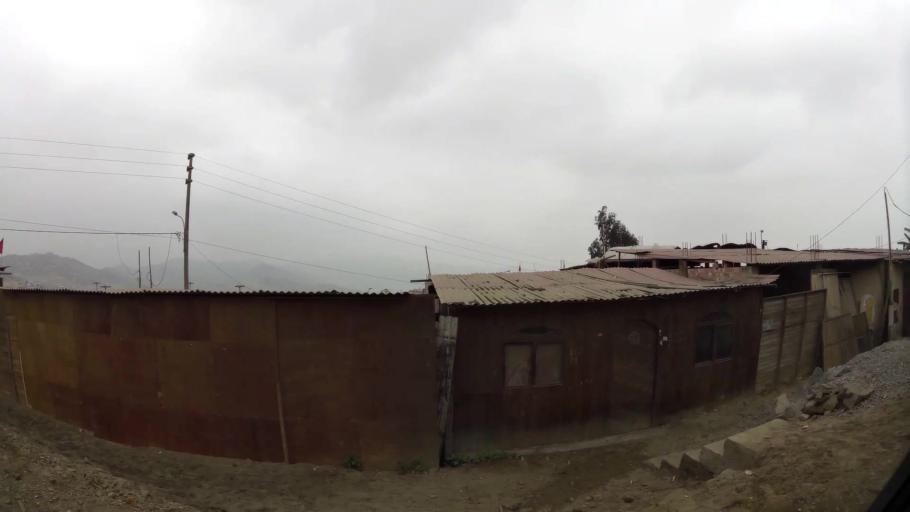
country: PE
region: Lima
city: Ventanilla
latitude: -11.8469
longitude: -77.1309
